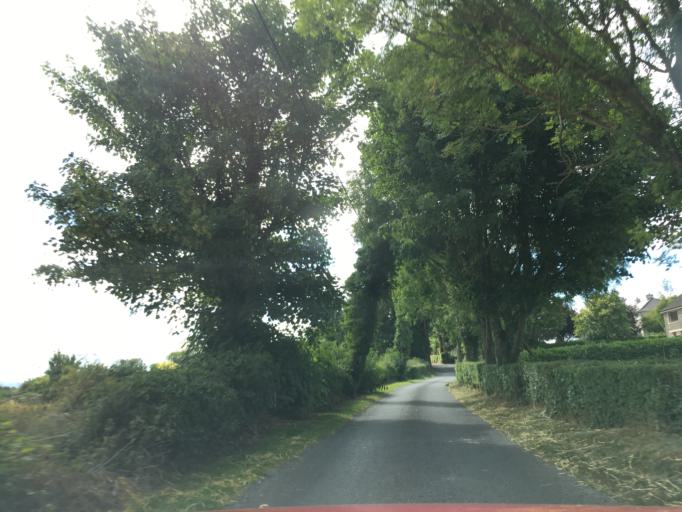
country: IE
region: Munster
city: Cashel
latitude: 52.4963
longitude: -7.9042
